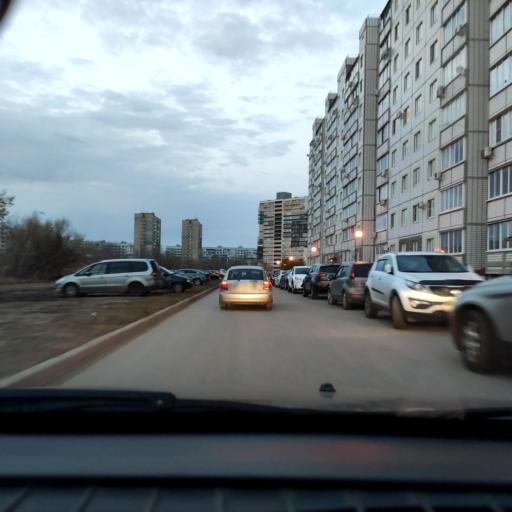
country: RU
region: Samara
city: Tol'yatti
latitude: 53.5244
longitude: 49.3335
